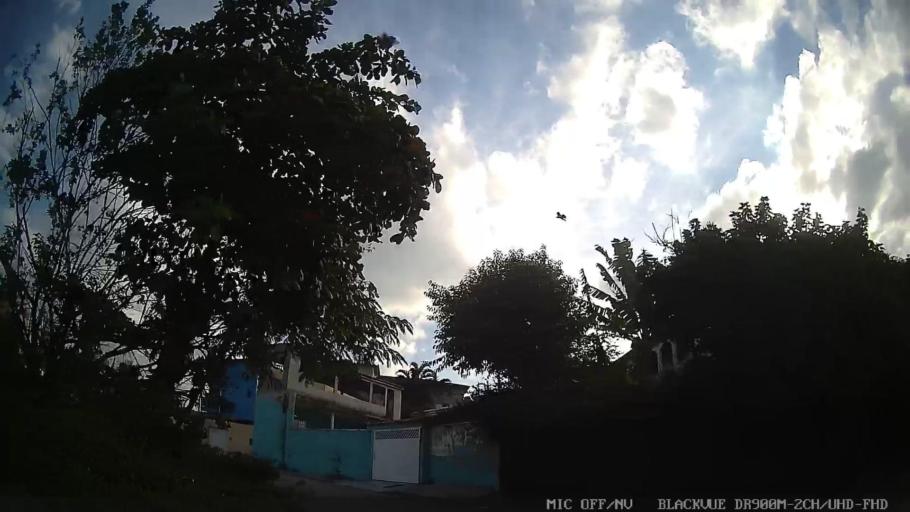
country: BR
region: Sao Paulo
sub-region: Guaruja
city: Guaruja
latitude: -23.9810
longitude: -46.2371
